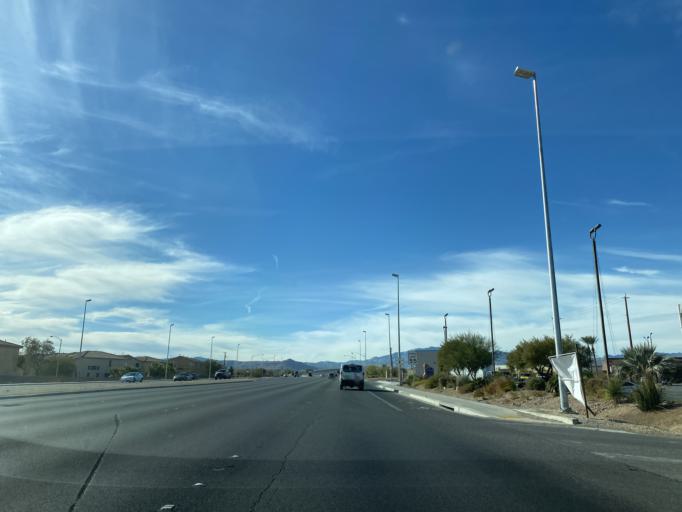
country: US
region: Nevada
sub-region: Clark County
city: Enterprise
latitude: 36.0299
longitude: -115.2143
